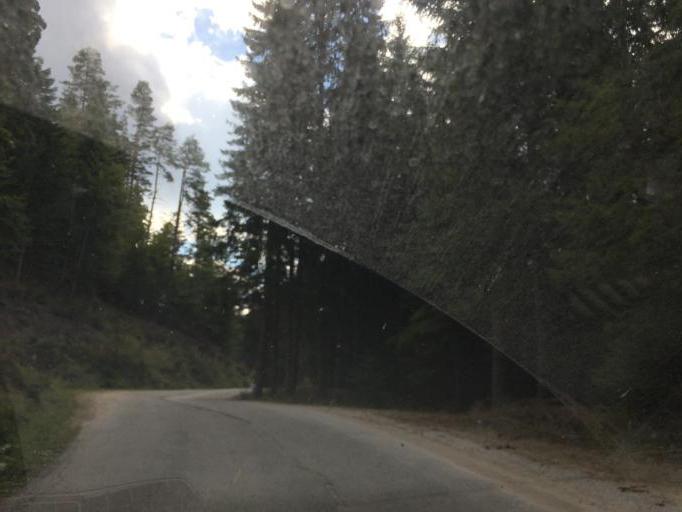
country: BG
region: Pazardzhik
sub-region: Obshtina Batak
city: Batak
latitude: 41.9105
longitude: 24.2910
